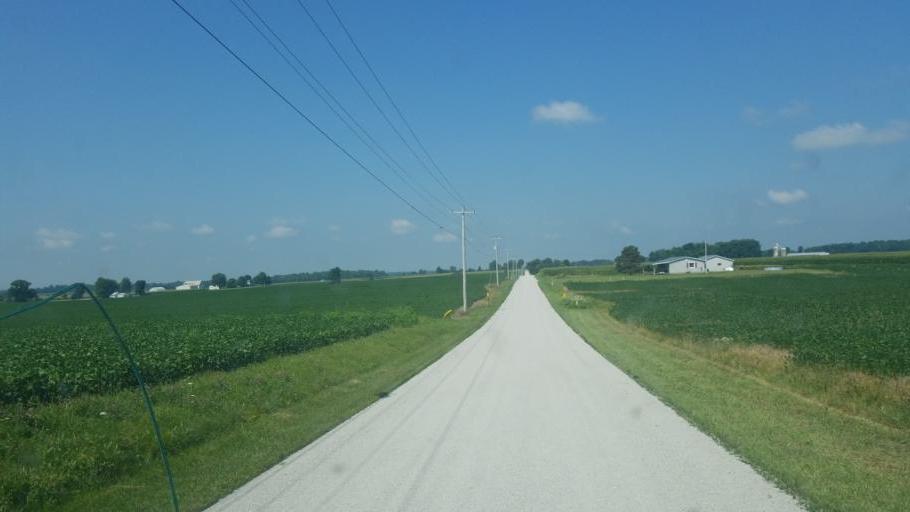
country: US
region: Ohio
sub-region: Hardin County
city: Kenton
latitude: 40.7037
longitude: -83.7131
